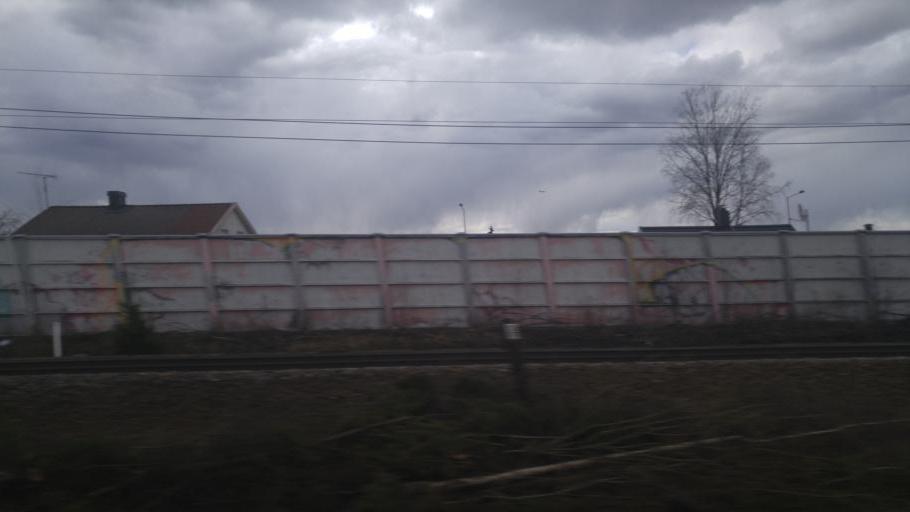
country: NO
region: Akershus
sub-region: Ullensaker
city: Klofta
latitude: 60.1003
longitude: 11.1413
